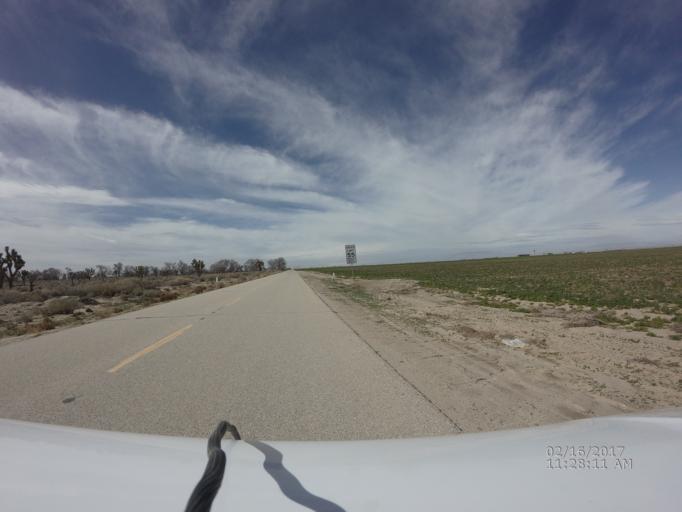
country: US
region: California
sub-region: Los Angeles County
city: Lake Los Angeles
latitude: 34.7048
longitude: -117.9169
